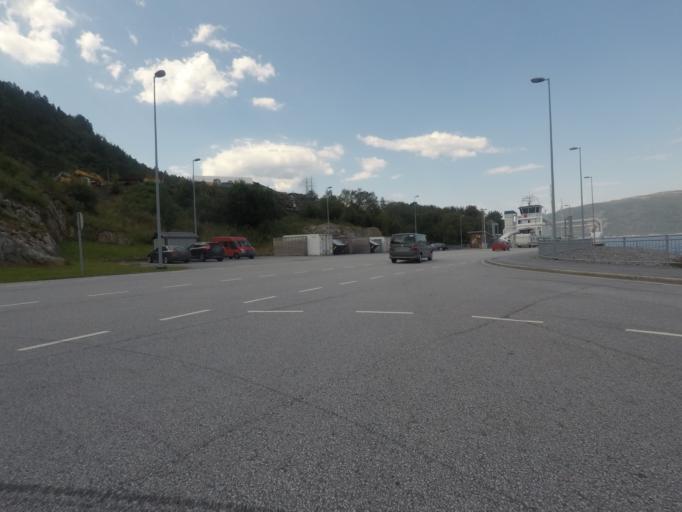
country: NO
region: Sogn og Fjordane
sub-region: Hyllestad
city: Hyllestad
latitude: 61.0544
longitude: 5.5055
